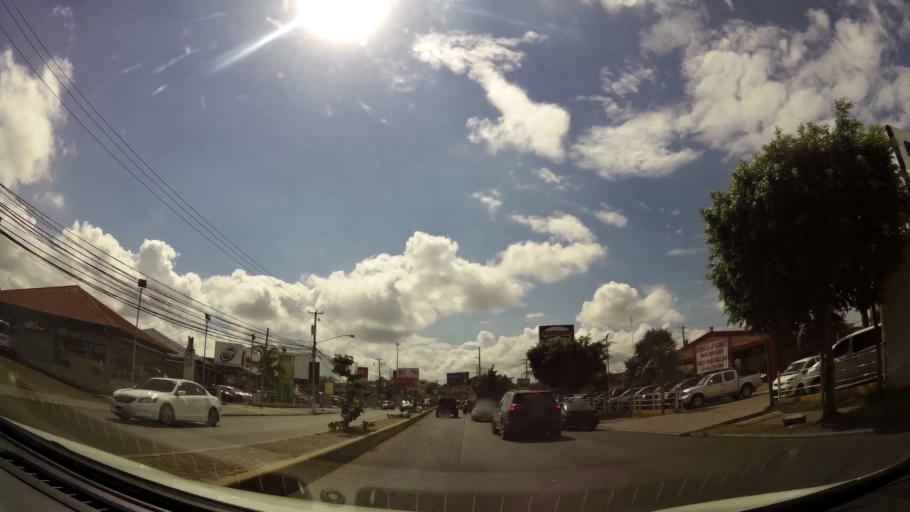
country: DO
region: Santiago
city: Santiago de los Caballeros
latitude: 19.4724
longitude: -70.6927
